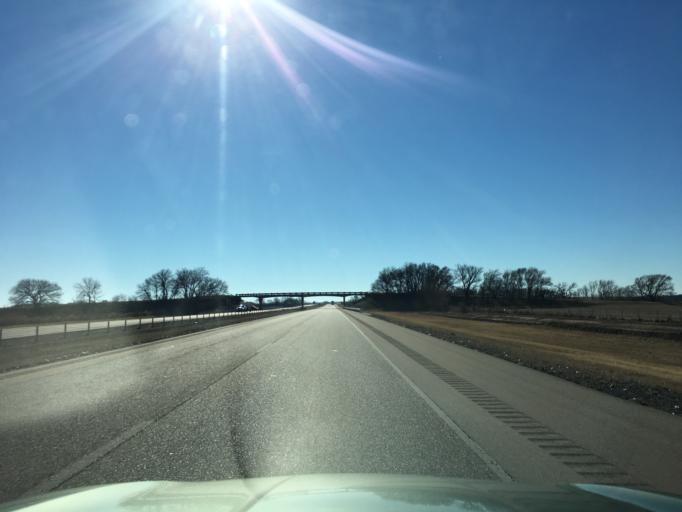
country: US
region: Oklahoma
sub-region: Kay County
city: Blackwell
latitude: 36.9150
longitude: -97.3517
